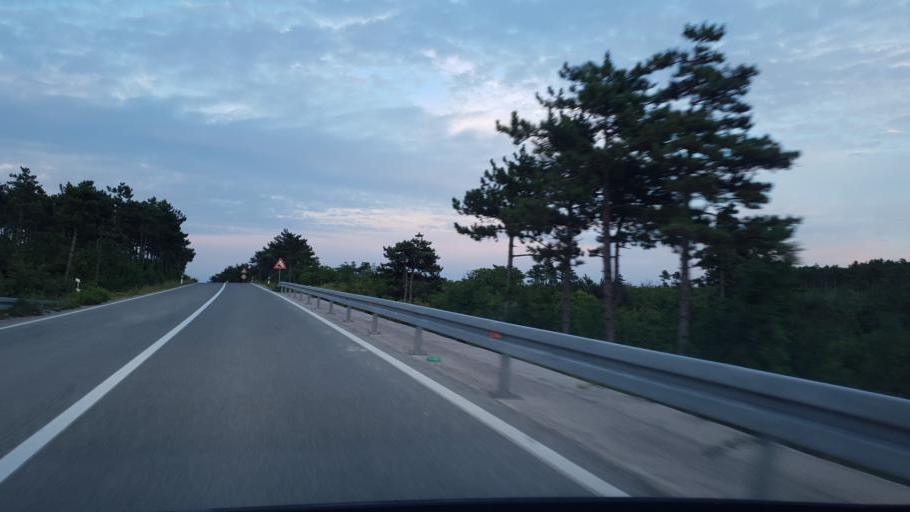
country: HR
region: Primorsko-Goranska
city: Punat
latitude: 45.0300
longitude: 14.6691
